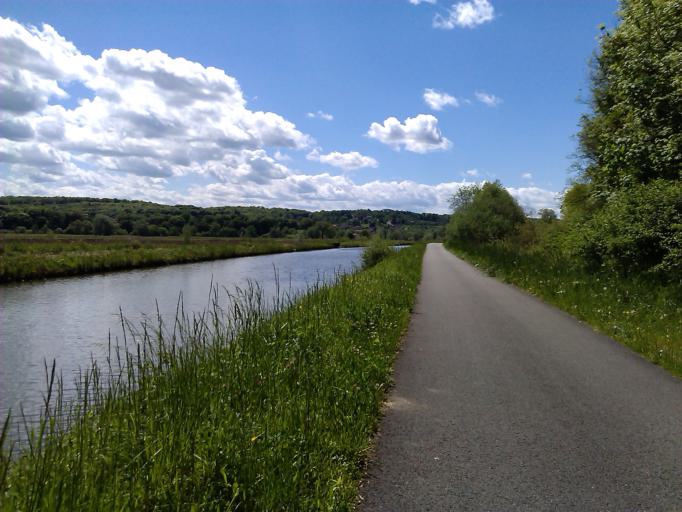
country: FR
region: Franche-Comte
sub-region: Territoire de Belfort
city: Mezire
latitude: 47.5355
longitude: 6.9081
